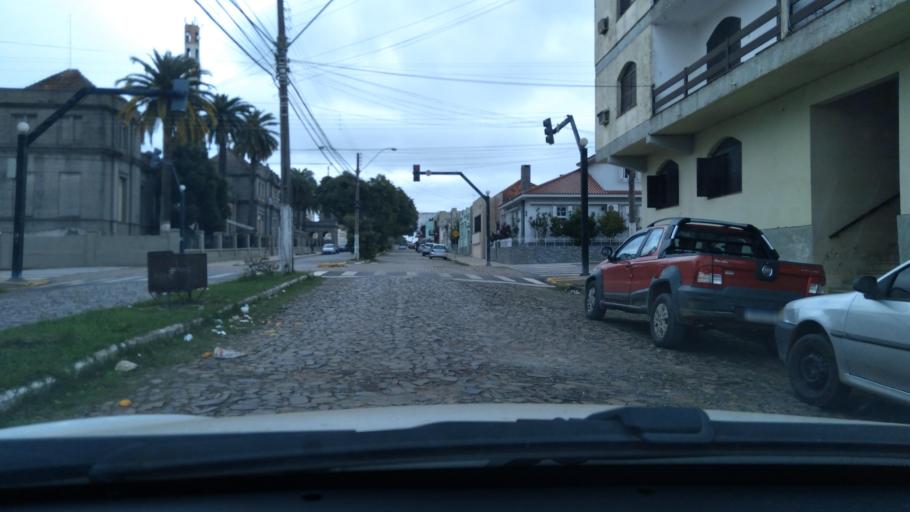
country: BR
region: Rio Grande do Sul
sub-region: Dom Pedrito
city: Dom Pedrito
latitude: -30.9853
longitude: -54.6711
